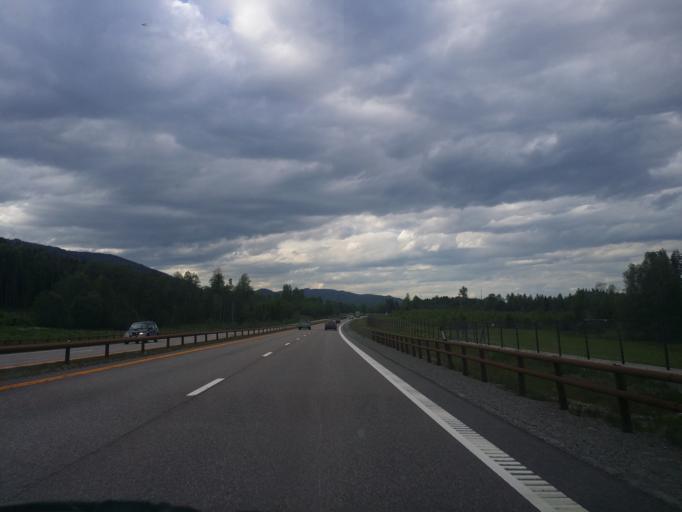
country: NO
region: Akershus
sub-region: Eidsvoll
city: Eidsvoll
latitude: 60.3574
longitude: 11.2059
